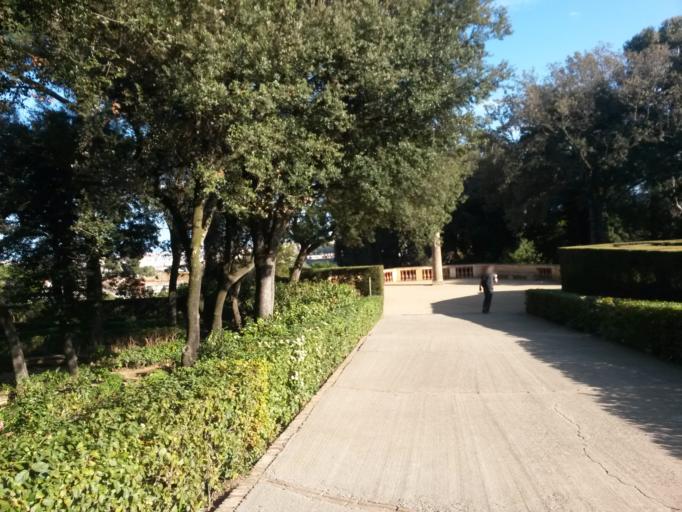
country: ES
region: Catalonia
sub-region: Provincia de Barcelona
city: Horta-Guinardo
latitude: 41.4405
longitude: 2.1459
